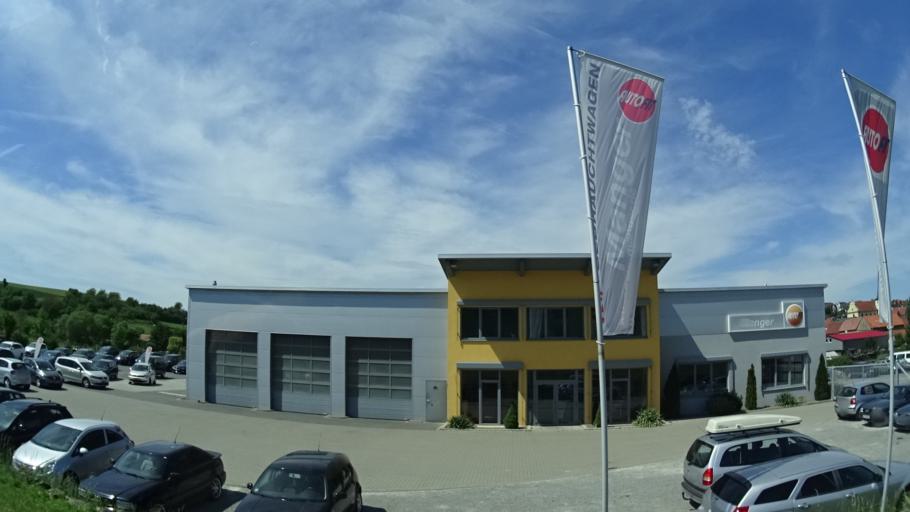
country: DE
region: Bavaria
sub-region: Regierungsbezirk Unterfranken
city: Arnstein
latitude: 50.0163
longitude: 10.0030
